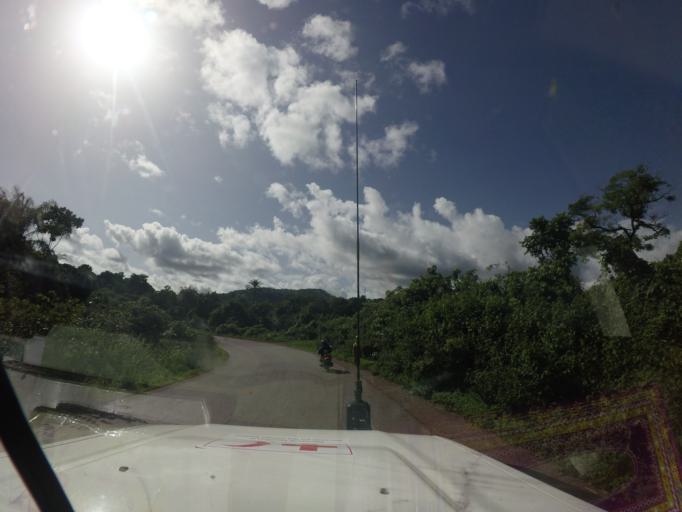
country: GN
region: Mamou
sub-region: Mamou Prefecture
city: Mamou
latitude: 10.3081
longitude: -12.2884
